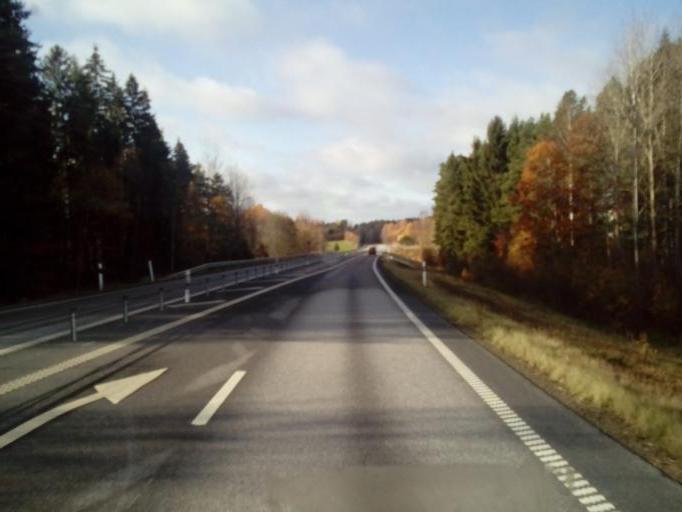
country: SE
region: Kalmar
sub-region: Vimmerby Kommun
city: Vimmerby
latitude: 57.6683
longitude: 15.9171
